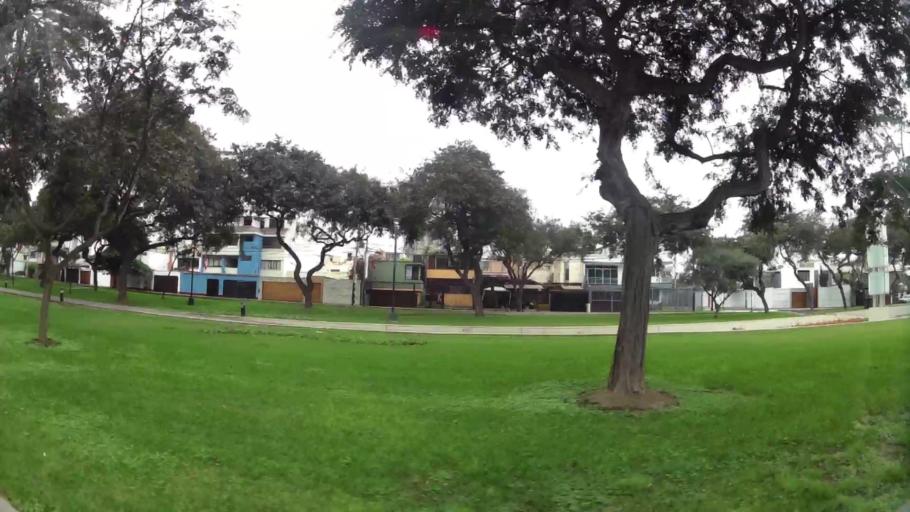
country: PE
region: Lima
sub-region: Lima
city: San Luis
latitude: -12.1004
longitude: -77.0181
